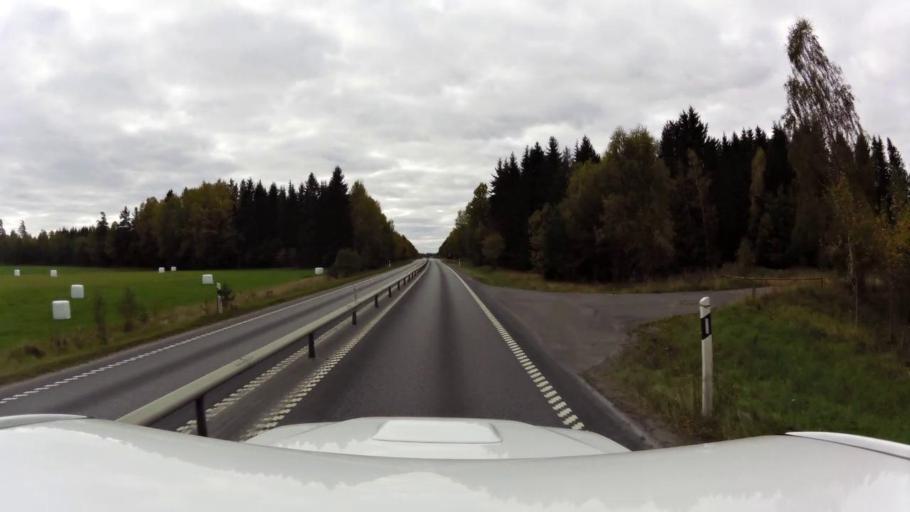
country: SE
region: OEstergoetland
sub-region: Linkopings Kommun
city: Malmslatt
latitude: 58.3808
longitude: 15.5423
